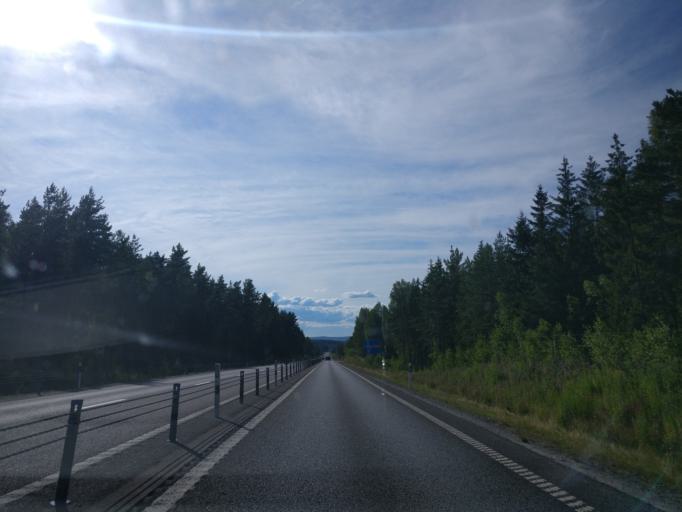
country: SE
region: Vaermland
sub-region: Arvika Kommun
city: Arvika
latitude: 59.6482
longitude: 12.6894
